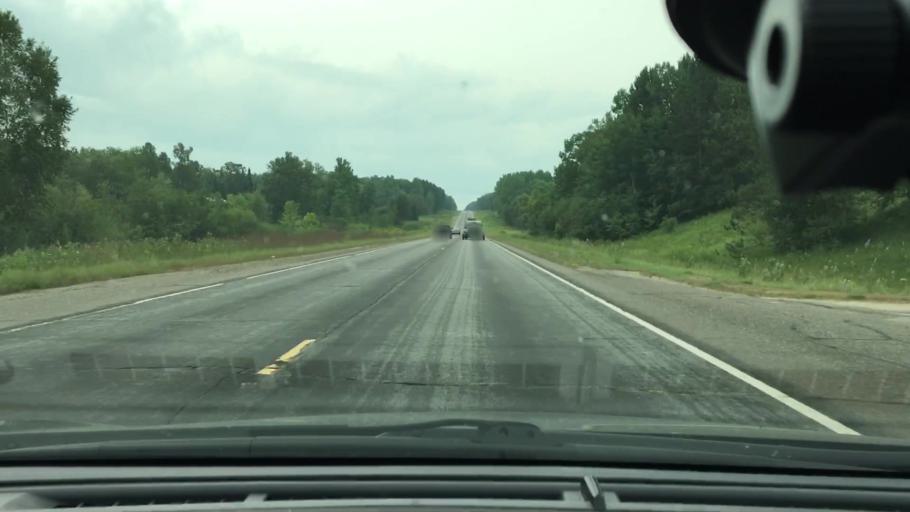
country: US
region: Minnesota
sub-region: Crow Wing County
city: Cross Lake
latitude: 46.6504
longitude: -93.9538
